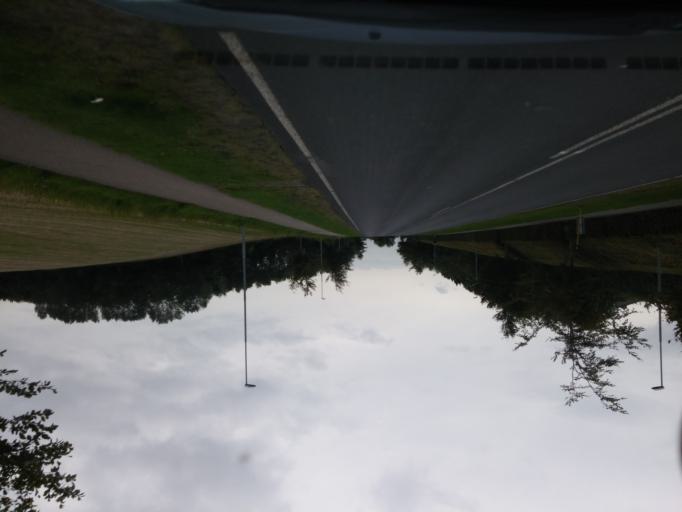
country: DK
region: South Denmark
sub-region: Kerteminde Kommune
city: Munkebo
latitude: 55.4511
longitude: 10.5408
